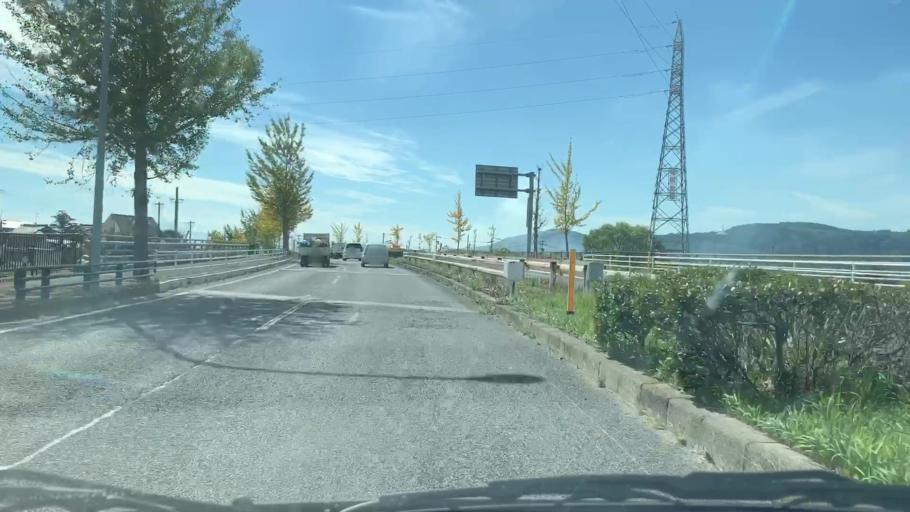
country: JP
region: Saga Prefecture
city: Saga-shi
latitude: 33.2562
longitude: 130.2003
